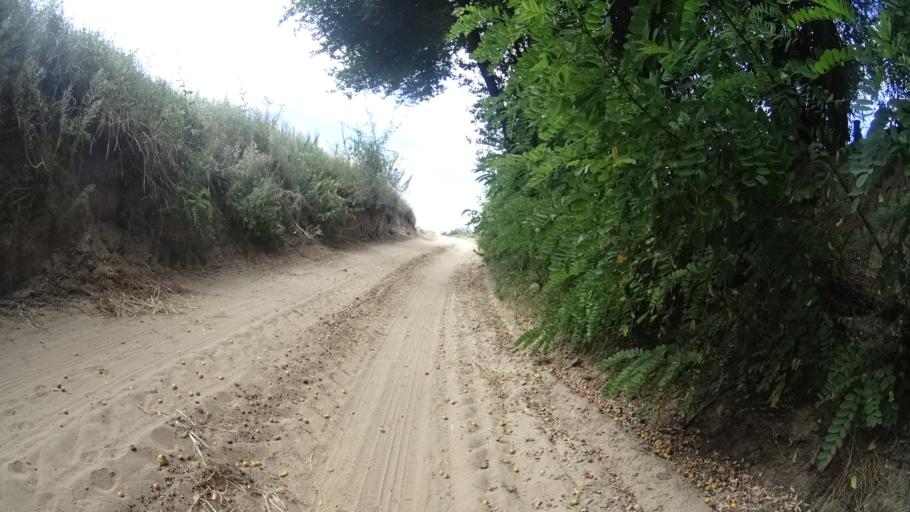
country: PL
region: Masovian Voivodeship
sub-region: Powiat bialobrzeski
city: Wysmierzyce
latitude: 51.6564
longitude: 20.8207
